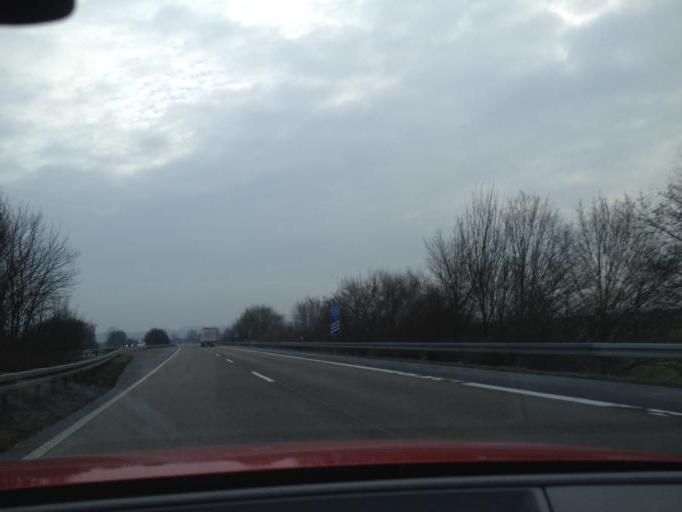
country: DE
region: Hesse
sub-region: Regierungsbezirk Darmstadt
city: Altenstadt
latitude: 50.2966
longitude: 8.9629
